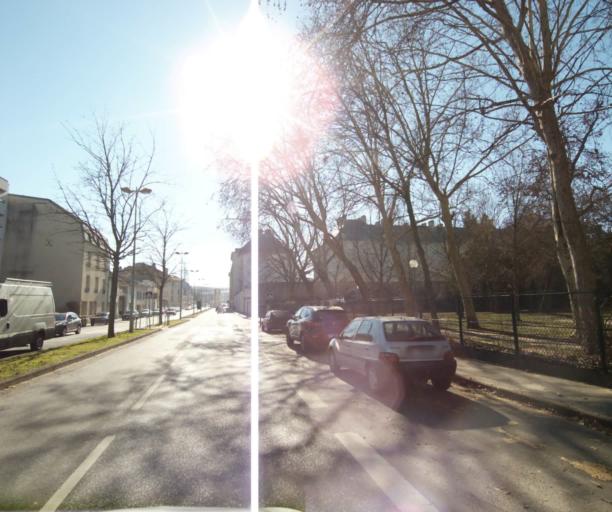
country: FR
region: Lorraine
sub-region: Departement de Meurthe-et-Moselle
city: Nancy
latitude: 48.6975
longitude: 6.1886
